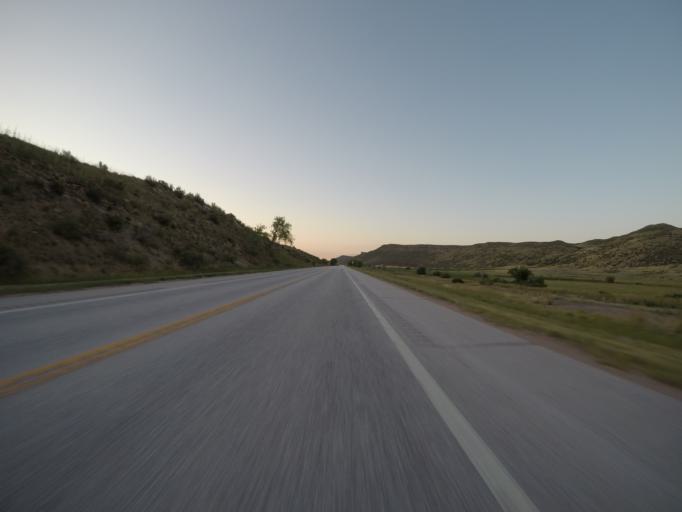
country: US
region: Colorado
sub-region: Larimer County
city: Laporte
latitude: 40.6790
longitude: -105.1785
